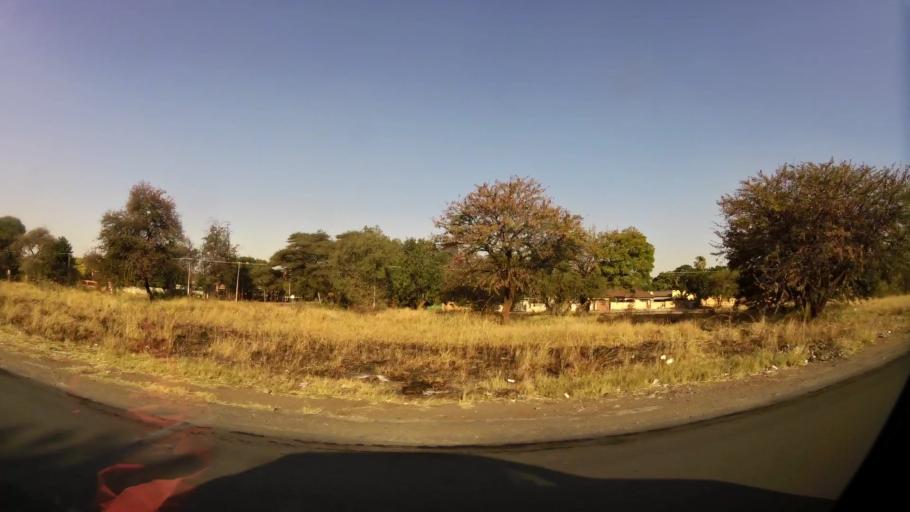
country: ZA
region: North-West
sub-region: Bojanala Platinum District Municipality
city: Rustenburg
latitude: -25.6497
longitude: 27.2241
